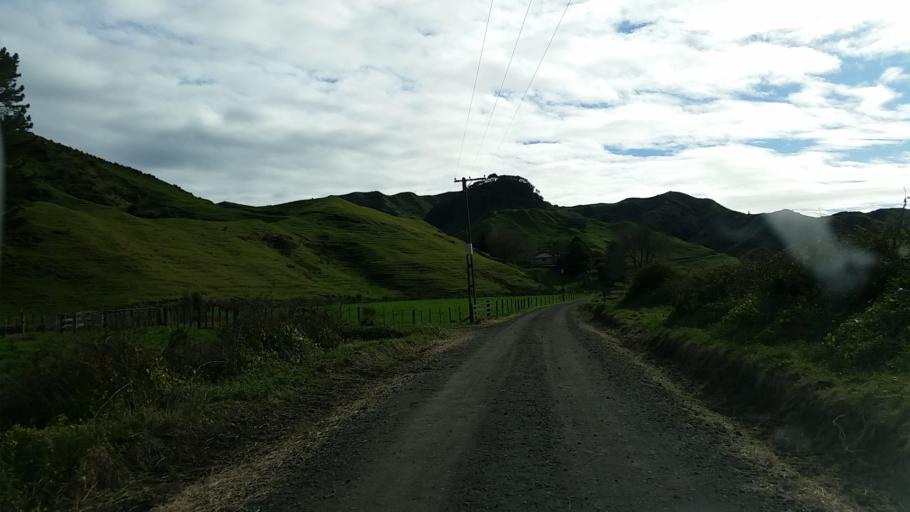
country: NZ
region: Taranaki
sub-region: South Taranaki District
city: Eltham
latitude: -39.2257
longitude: 174.5633
